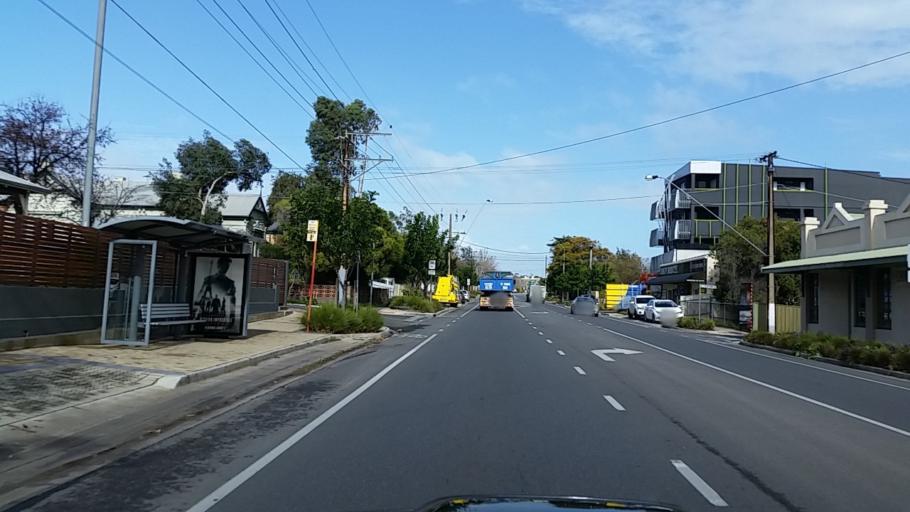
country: AU
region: South Australia
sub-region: Prospect
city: Prospect
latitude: -34.8935
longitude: 138.5854
